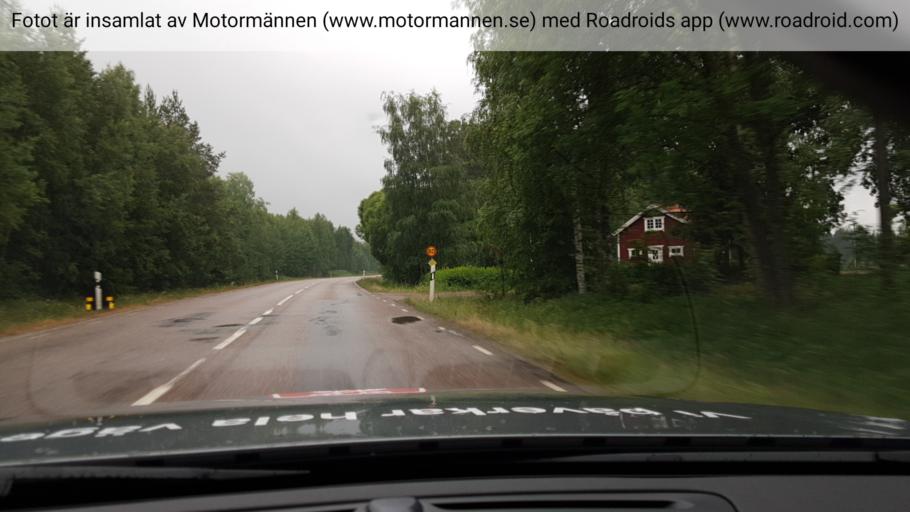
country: SE
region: Vaestmanland
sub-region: Norbergs Kommun
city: Norberg
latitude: 60.0311
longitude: 15.9923
